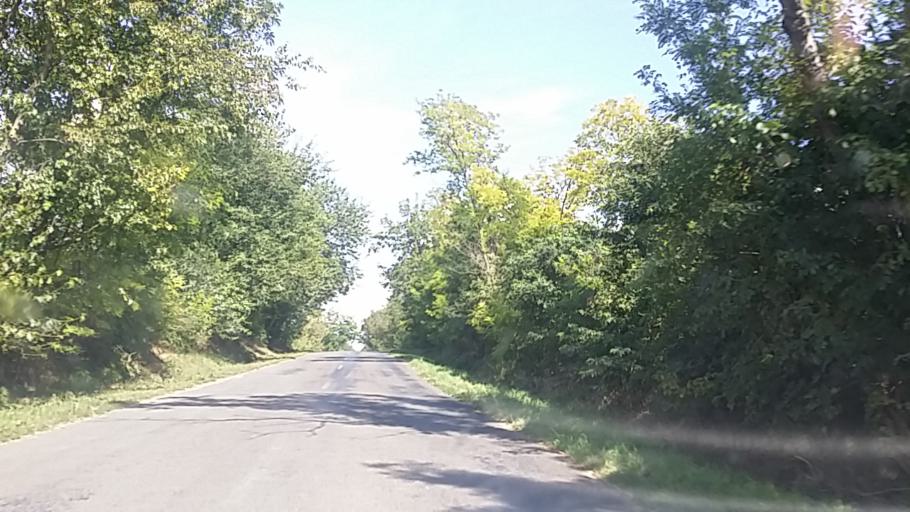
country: HU
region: Tolna
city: Hogyesz
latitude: 46.5269
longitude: 18.4330
